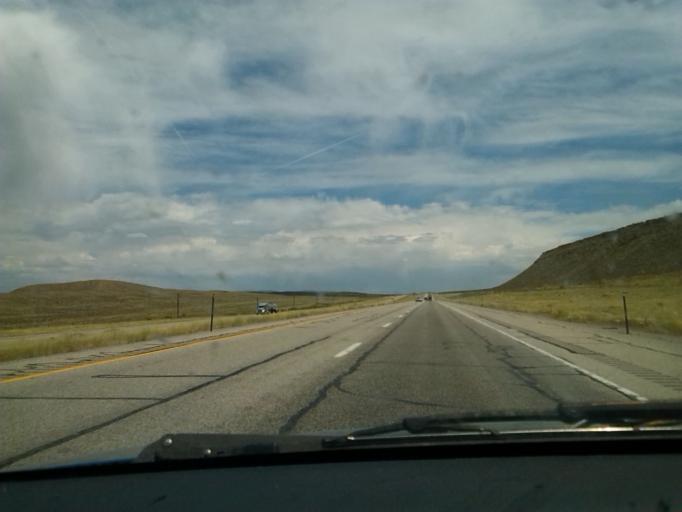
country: US
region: Wyoming
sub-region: Carbon County
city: Saratoga
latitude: 41.7438
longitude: -106.9025
